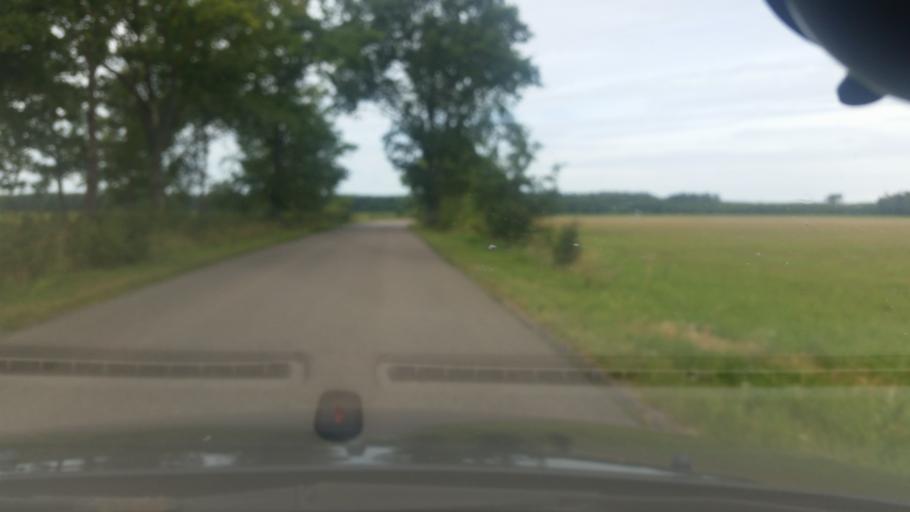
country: PL
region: Pomeranian Voivodeship
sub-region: Powiat leborski
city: Leba
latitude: 54.7325
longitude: 17.6039
